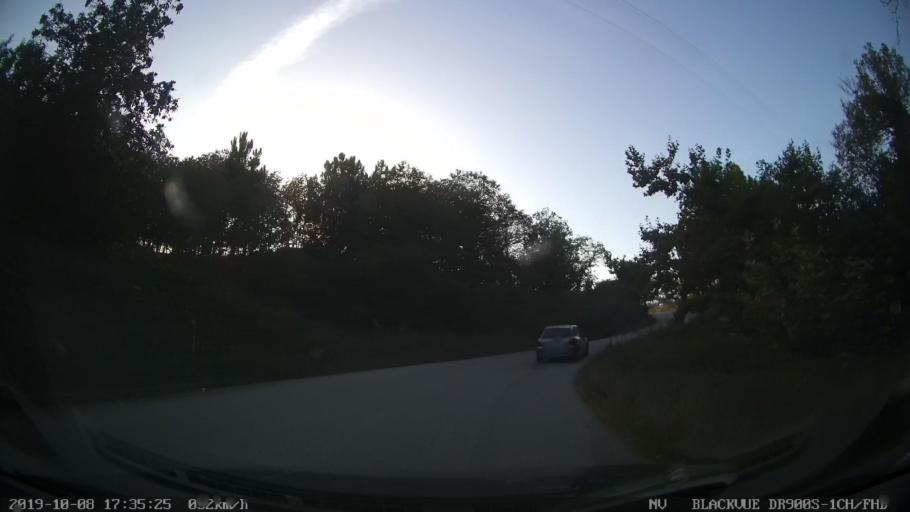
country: PT
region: Vila Real
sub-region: Sabrosa
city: Sabrosa
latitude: 41.2497
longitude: -7.5936
